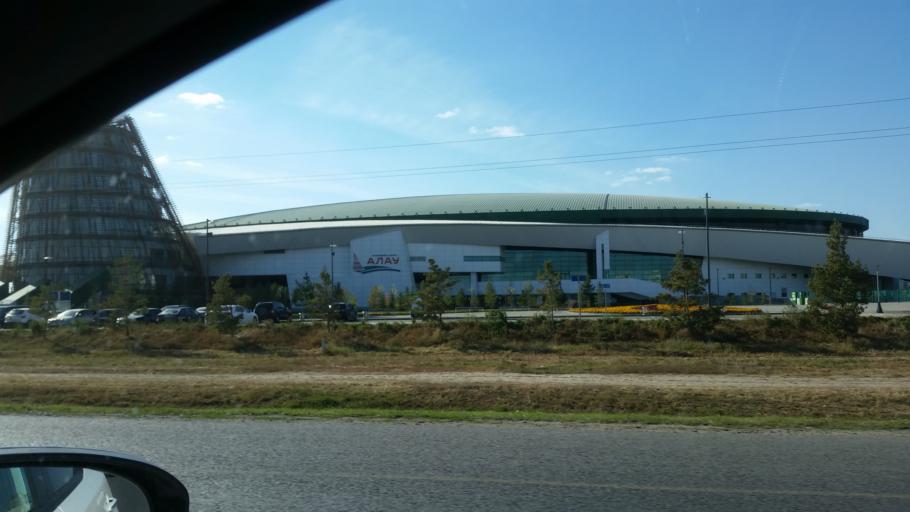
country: KZ
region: Astana Qalasy
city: Astana
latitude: 51.1050
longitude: 71.4082
